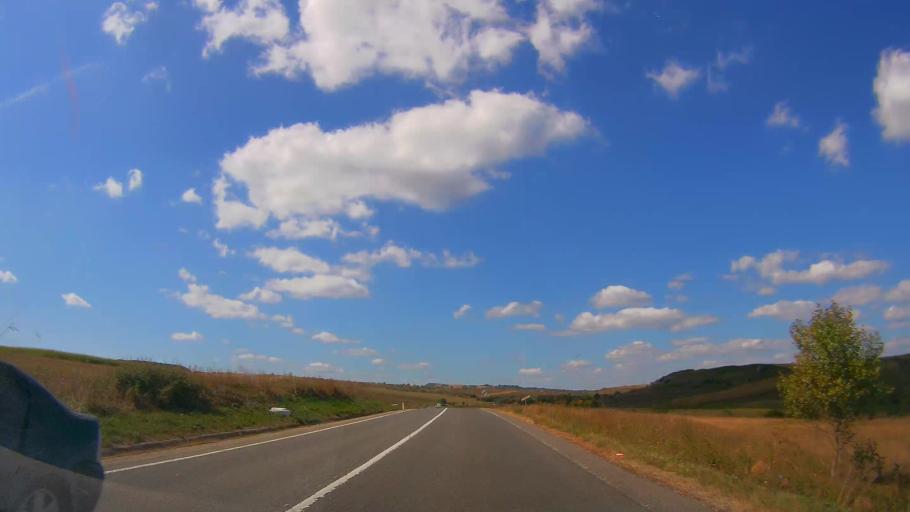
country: RO
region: Cluj
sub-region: Comuna Sanpaul
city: Sanpaul
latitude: 46.9219
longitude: 23.4178
